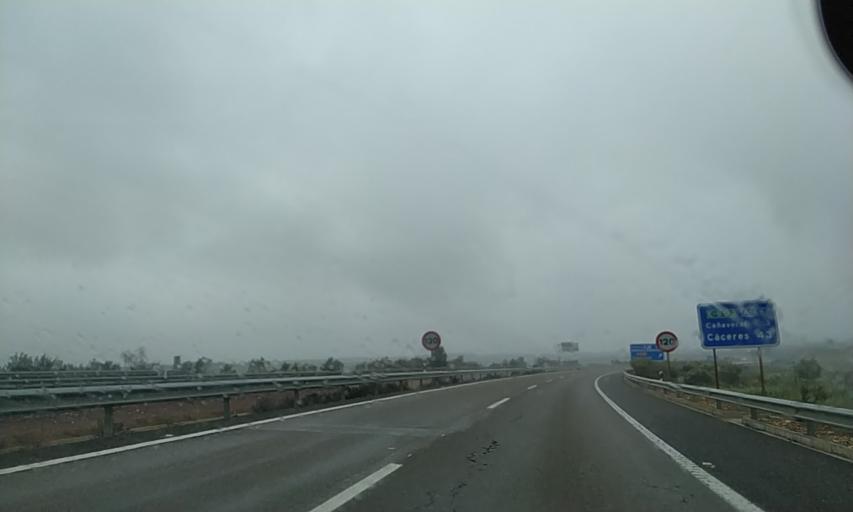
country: ES
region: Extremadura
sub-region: Provincia de Caceres
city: Casas de Millan
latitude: 39.8123
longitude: -6.3626
